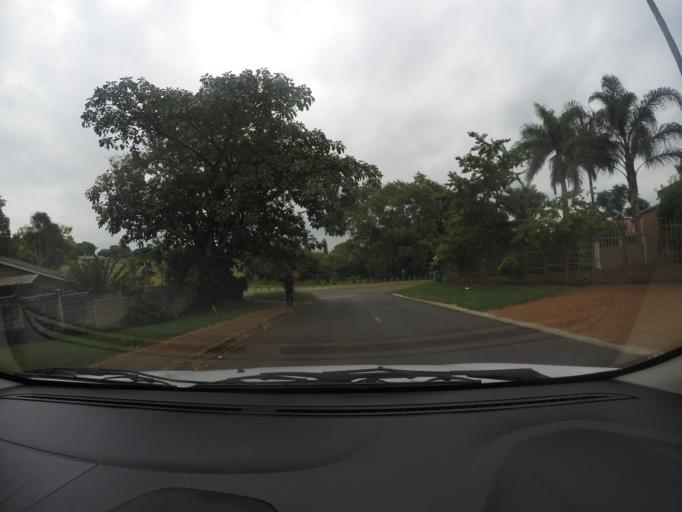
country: ZA
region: KwaZulu-Natal
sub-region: uThungulu District Municipality
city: Empangeni
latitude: -28.7379
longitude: 31.8975
